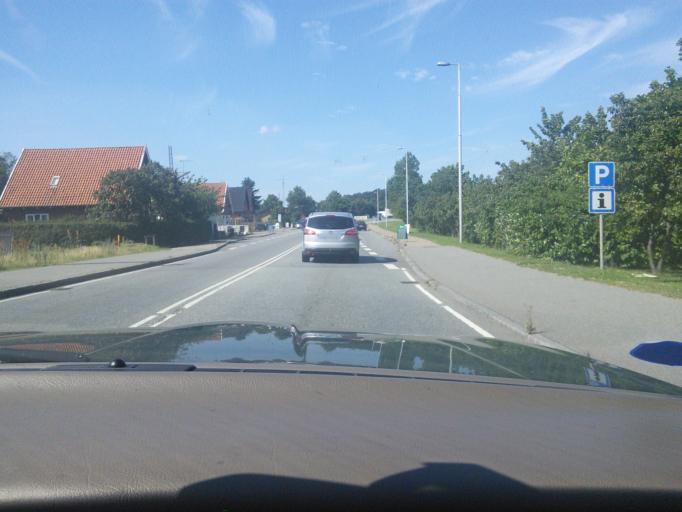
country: DK
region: Capital Region
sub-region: Halsnaes Kommune
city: Frederiksvaerk
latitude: 55.9650
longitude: 12.0298
